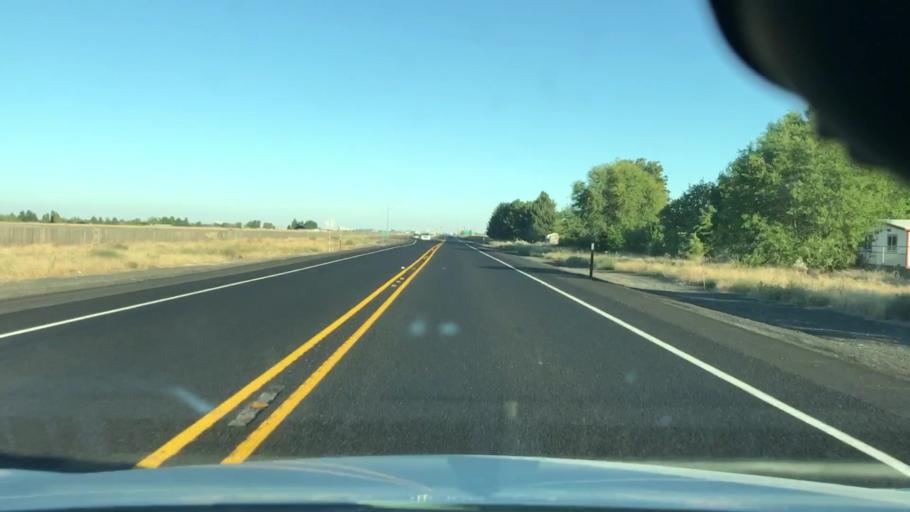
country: US
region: Washington
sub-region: Grant County
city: Cascade Valley
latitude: 47.1598
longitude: -119.3201
